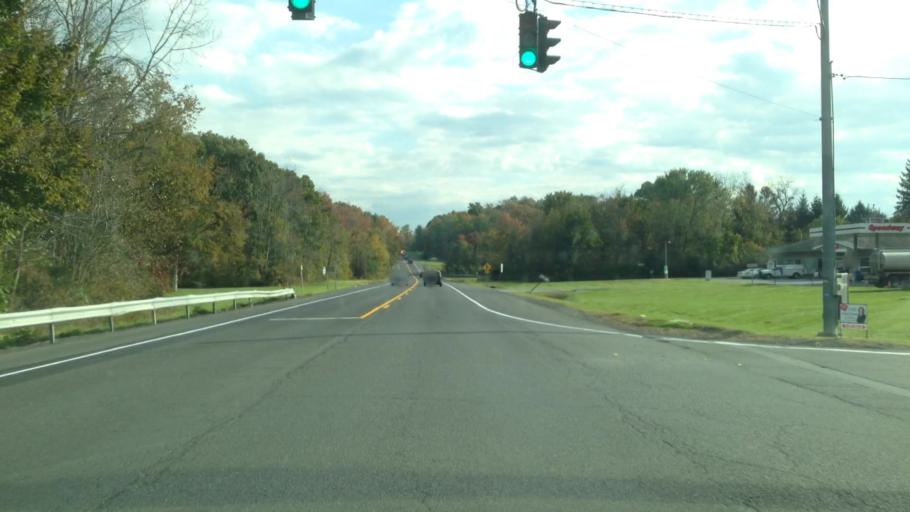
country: US
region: New York
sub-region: Ulster County
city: Clintondale
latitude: 41.7381
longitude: -74.0163
